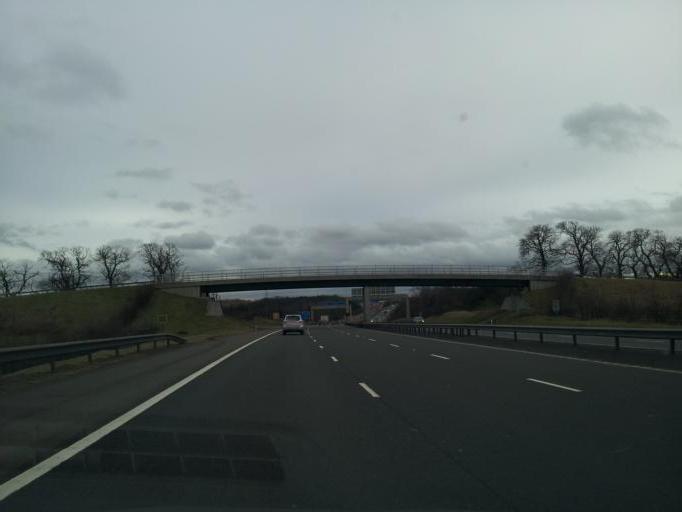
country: GB
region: England
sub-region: Staffordshire
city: Shenstone
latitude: 52.6341
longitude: -1.8060
